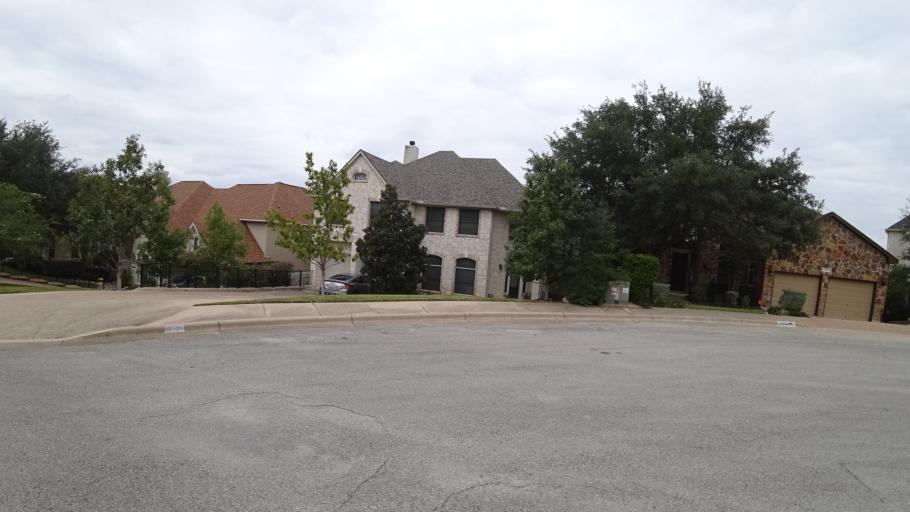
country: US
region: Texas
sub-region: Travis County
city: Bee Cave
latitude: 30.3136
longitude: -97.9225
